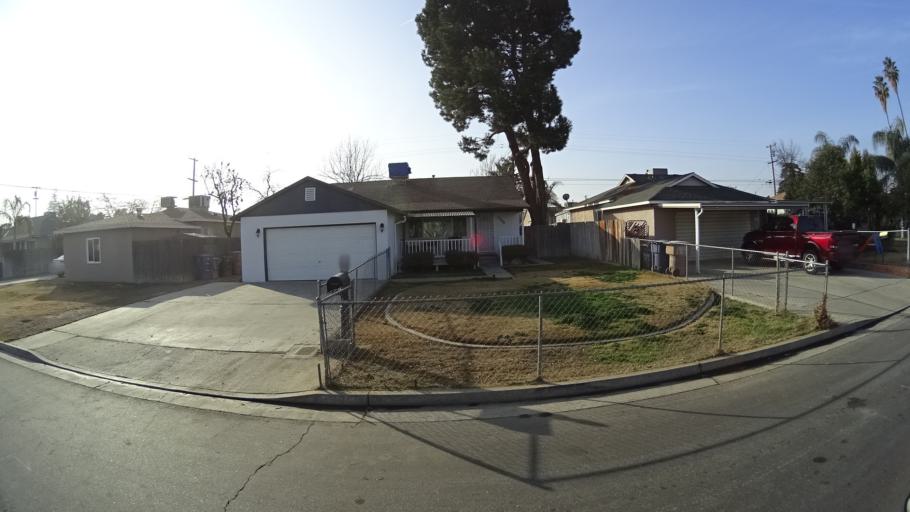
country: US
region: California
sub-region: Kern County
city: Bakersfield
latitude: 35.3362
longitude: -119.0240
